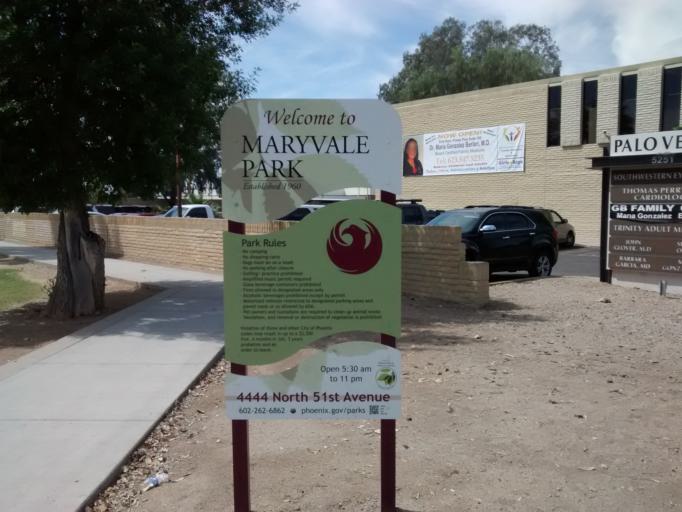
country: US
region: Arizona
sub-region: Maricopa County
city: Glendale
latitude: 33.5021
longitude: -112.1716
